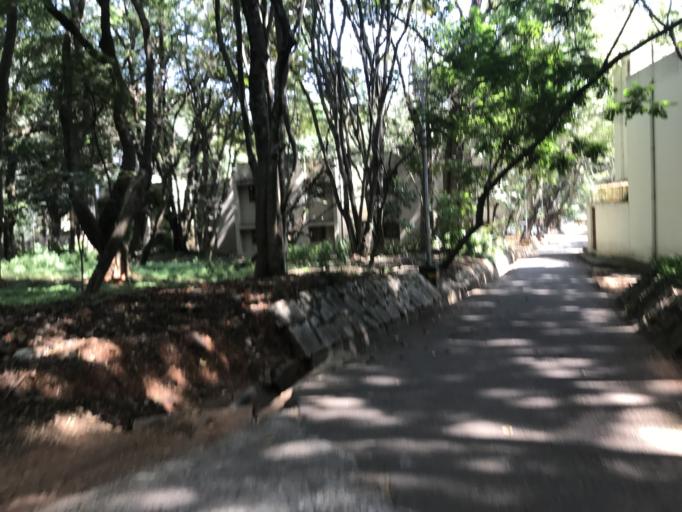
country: IN
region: Karnataka
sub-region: Bangalore Urban
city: Bangalore
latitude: 13.0234
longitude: 77.5667
